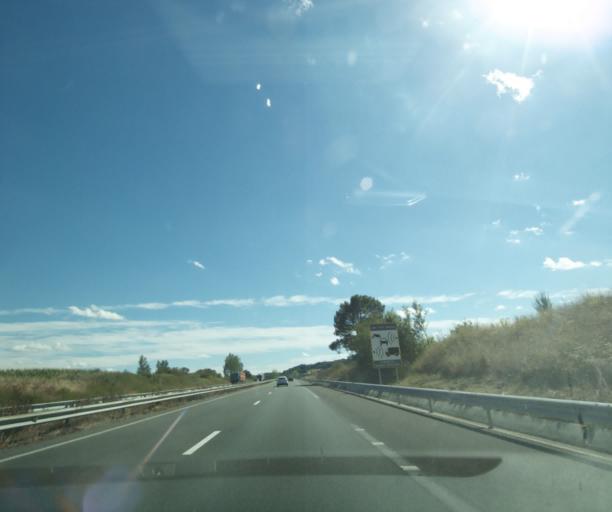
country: FR
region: Aquitaine
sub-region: Departement du Lot-et-Garonne
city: Damazan
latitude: 44.2767
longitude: 0.2721
